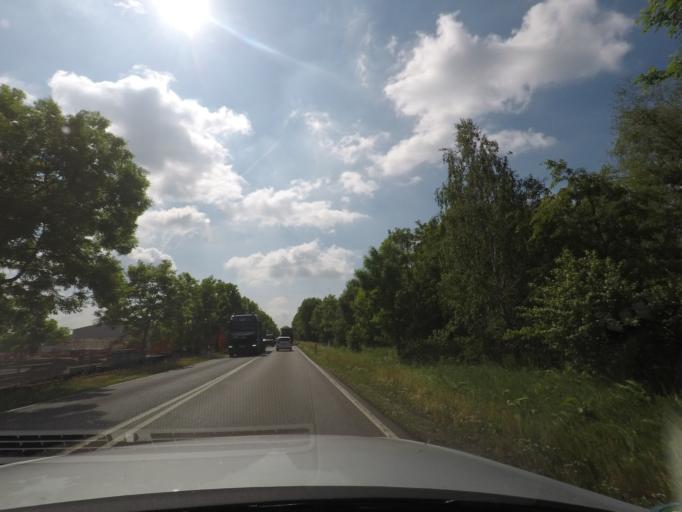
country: DE
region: Saxony
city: Markranstadt
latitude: 51.2859
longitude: 12.2451
